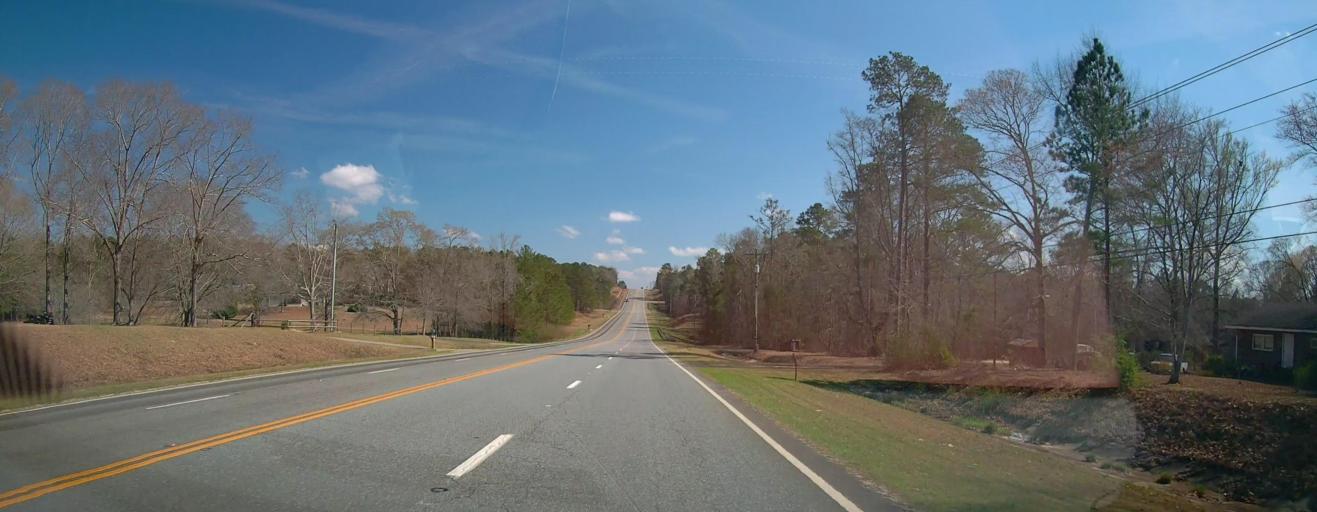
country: US
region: Georgia
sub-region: Wilkinson County
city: Gordon
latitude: 32.9159
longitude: -83.3880
